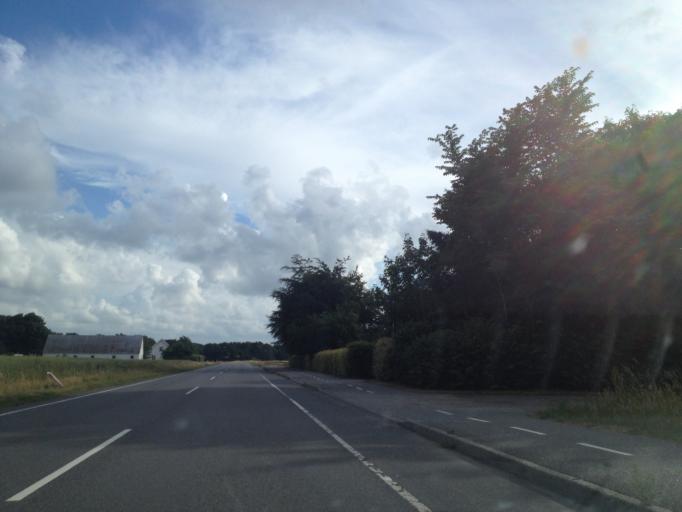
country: DK
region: South Denmark
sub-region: Vejen Kommune
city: Brorup
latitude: 55.4471
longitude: 9.0064
